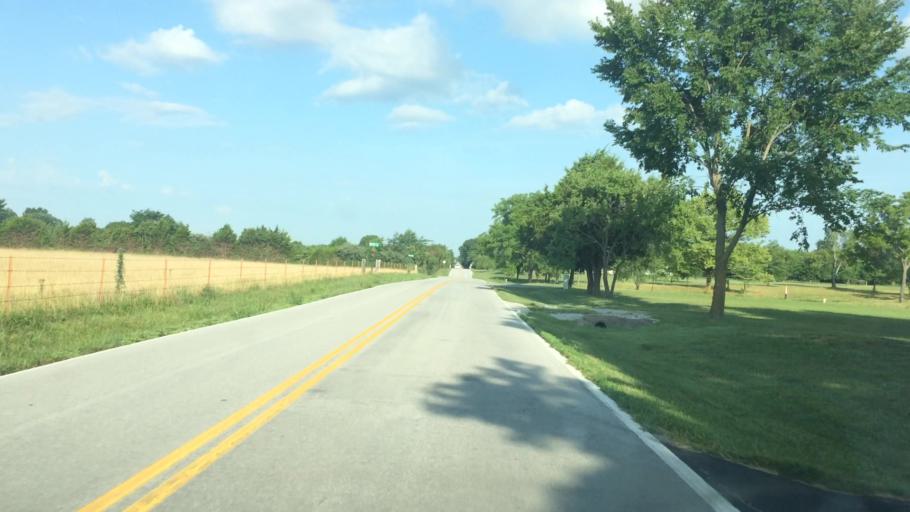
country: US
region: Missouri
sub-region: Greene County
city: Strafford
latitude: 37.2720
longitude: -93.1859
